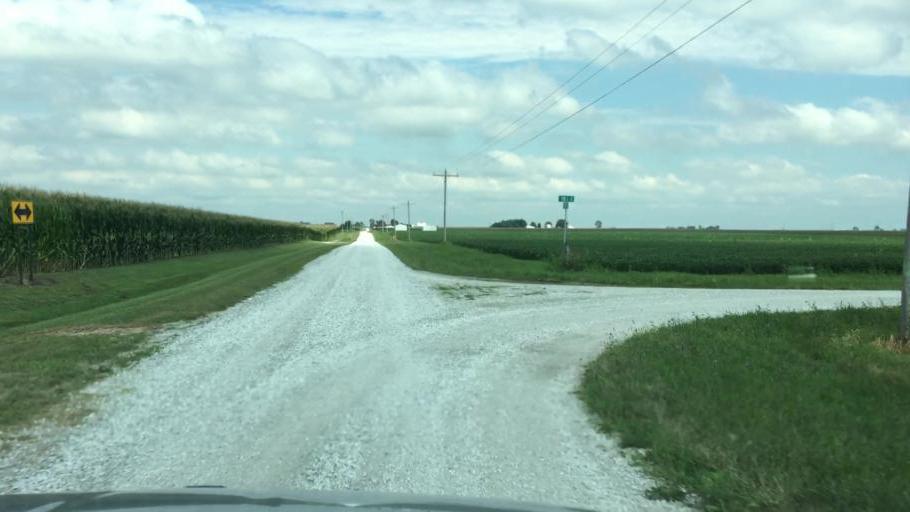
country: US
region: Illinois
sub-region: Hancock County
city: Nauvoo
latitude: 40.5215
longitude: -91.2886
